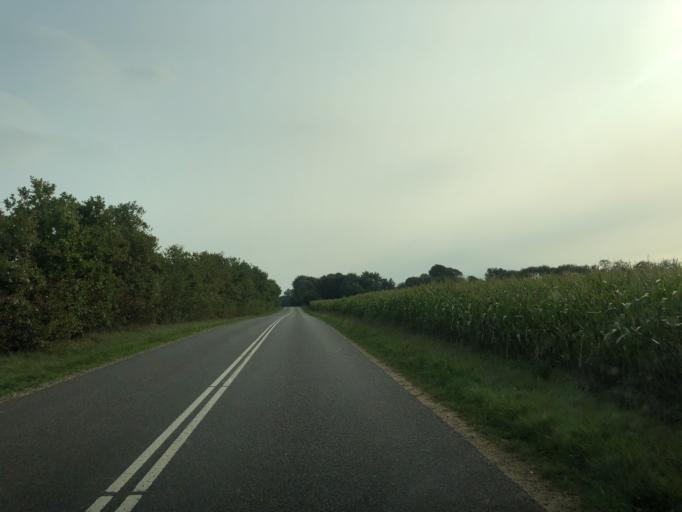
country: DK
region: Central Jutland
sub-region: Ringkobing-Skjern Kommune
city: Videbaek
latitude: 56.0755
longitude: 8.7031
